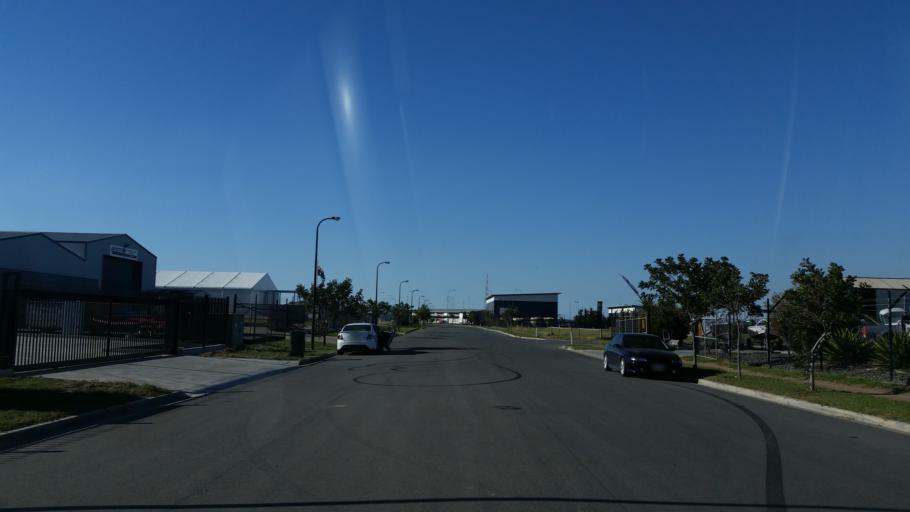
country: AU
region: South Australia
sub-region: Port Adelaide Enfield
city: Birkenhead
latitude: -34.8203
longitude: 138.5082
